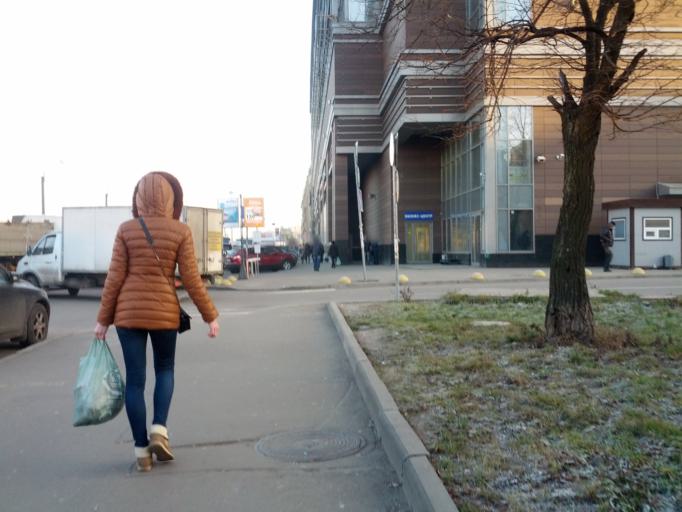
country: RU
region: St.-Petersburg
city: Centralniy
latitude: 59.9154
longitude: 30.3468
